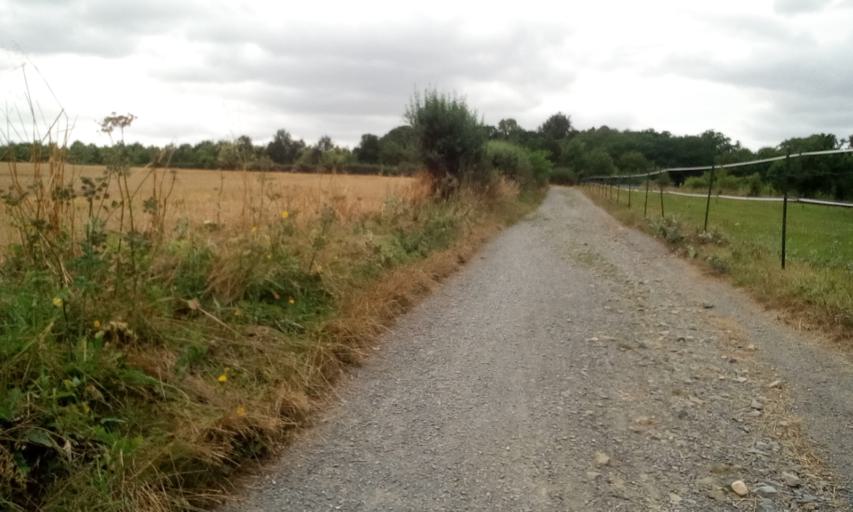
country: FR
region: Lower Normandy
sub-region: Departement du Calvados
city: Bretteville-sur-Odon
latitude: 49.1582
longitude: -0.4227
